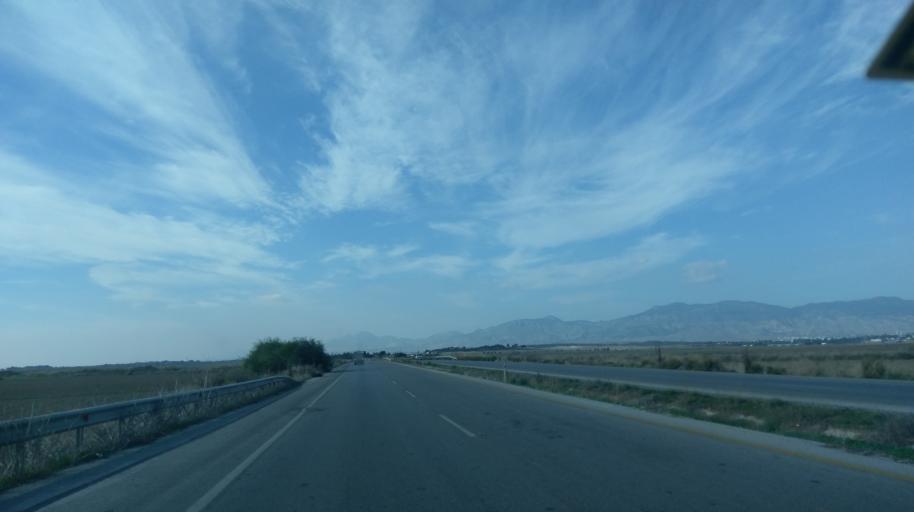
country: CY
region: Ammochostos
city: Lefkonoiko
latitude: 35.1883
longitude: 33.6317
